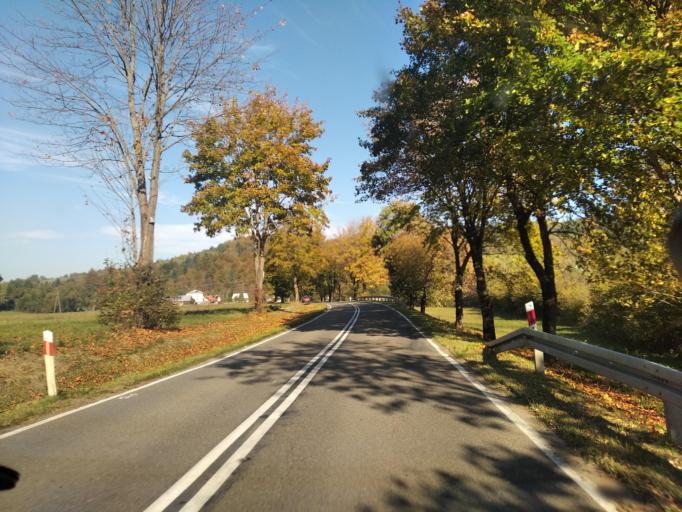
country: PL
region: Subcarpathian Voivodeship
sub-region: Powiat leski
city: Baligrod
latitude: 49.3847
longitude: 22.2845
